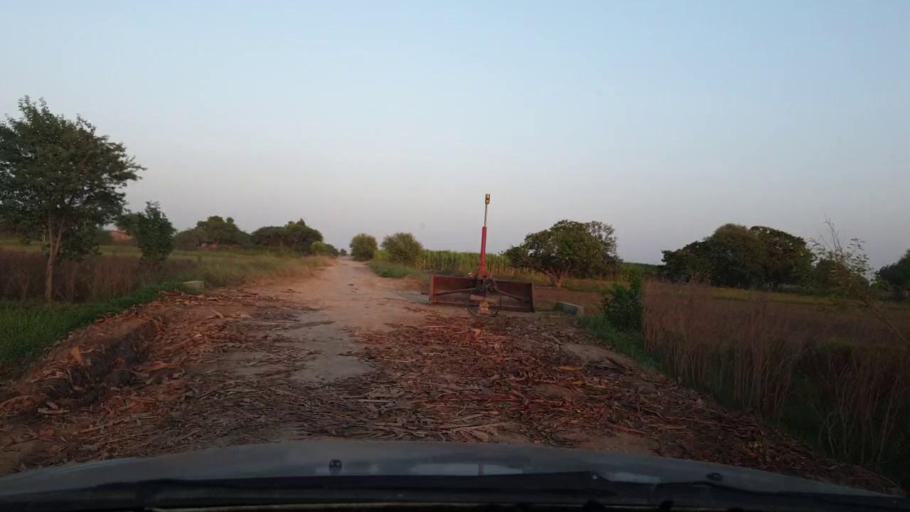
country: PK
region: Sindh
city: Tando Ghulam Ali
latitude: 25.0802
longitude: 68.9549
